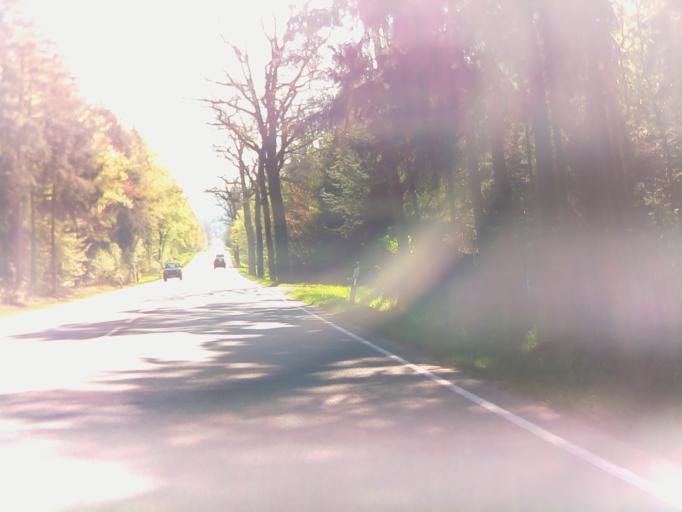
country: DE
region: Saxony
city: Mehltheuer
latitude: 50.5440
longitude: 12.0526
